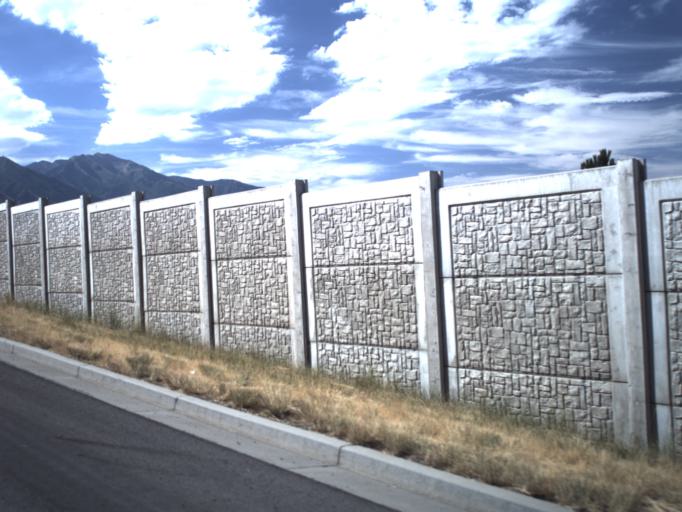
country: US
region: Utah
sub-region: Utah County
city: Spanish Fork
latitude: 40.1172
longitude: -111.6369
